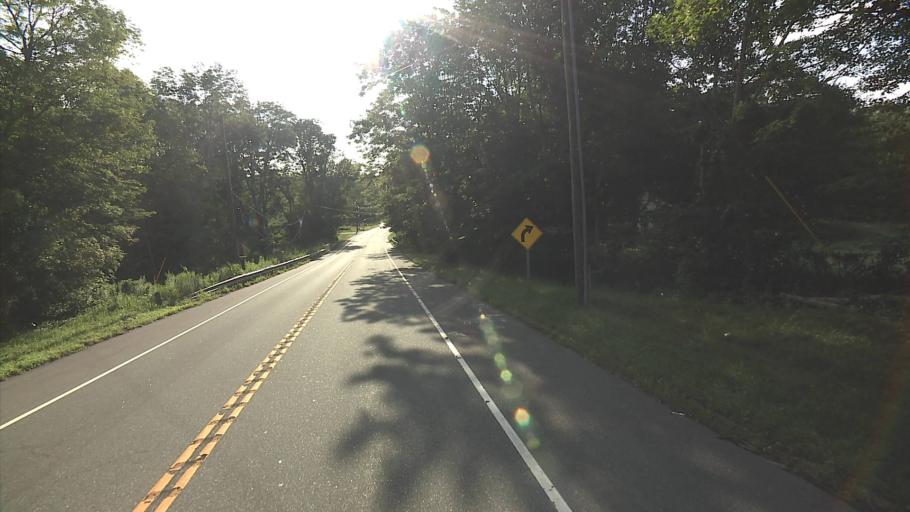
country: US
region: Connecticut
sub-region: New London County
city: Preston City
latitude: 41.4671
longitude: -71.9156
